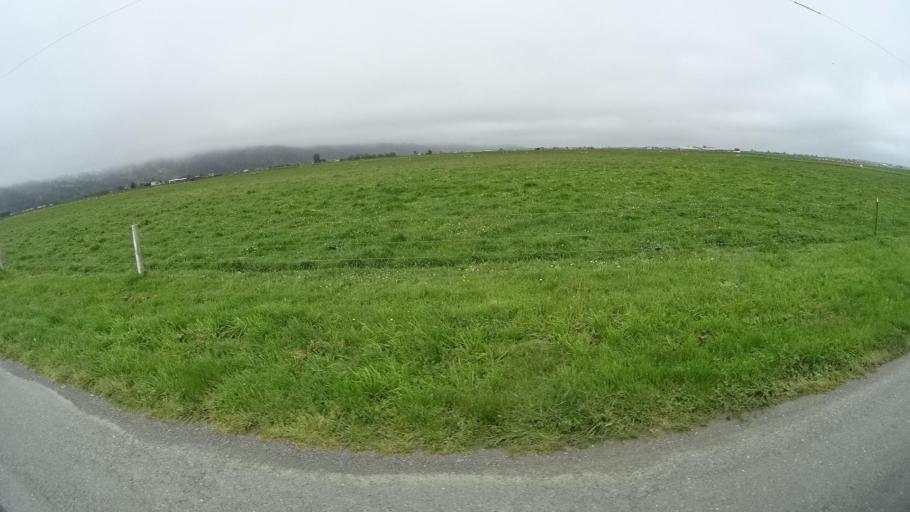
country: US
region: California
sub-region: Humboldt County
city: Fortuna
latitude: 40.5719
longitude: -124.1878
